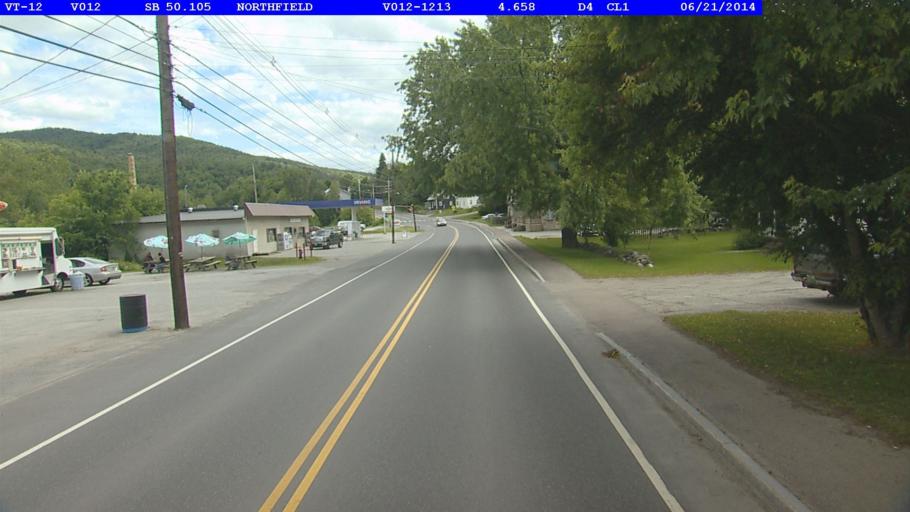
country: US
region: Vermont
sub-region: Washington County
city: Northfield
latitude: 44.1555
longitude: -72.6569
